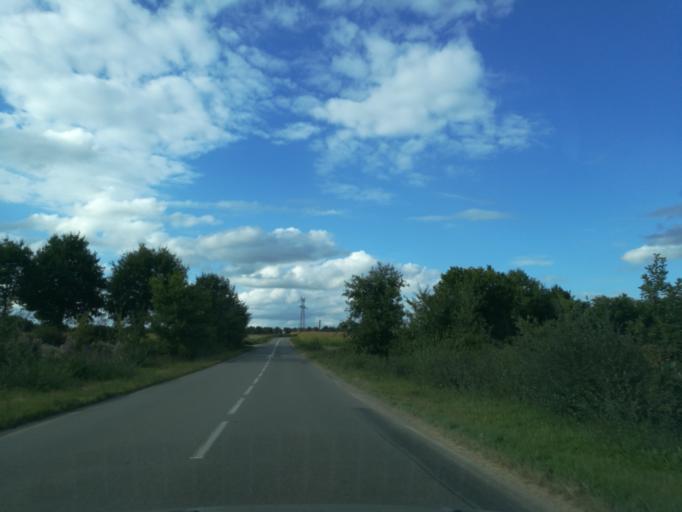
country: FR
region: Brittany
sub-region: Departement d'Ille-et-Vilaine
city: Montfort-sur-Meu
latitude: 48.1448
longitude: -1.9480
